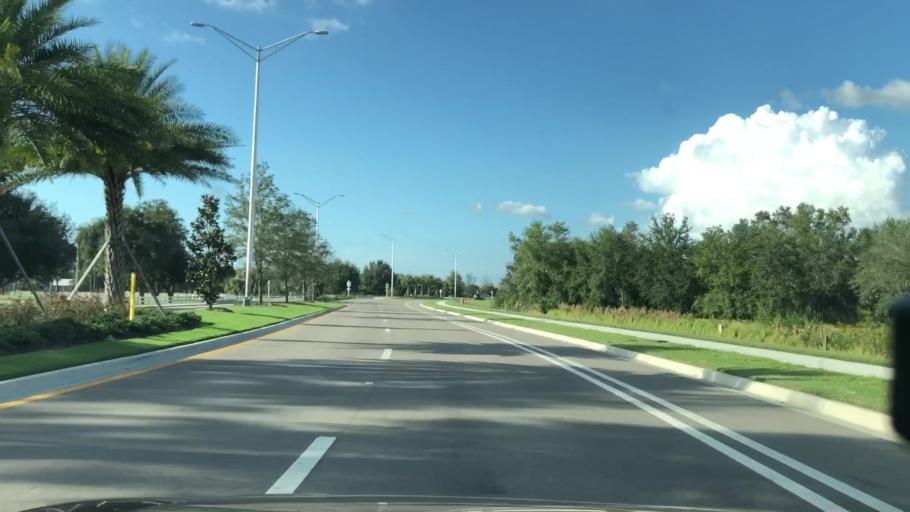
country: US
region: Florida
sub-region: Sarasota County
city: The Meadows
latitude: 27.3826
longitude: -82.3967
